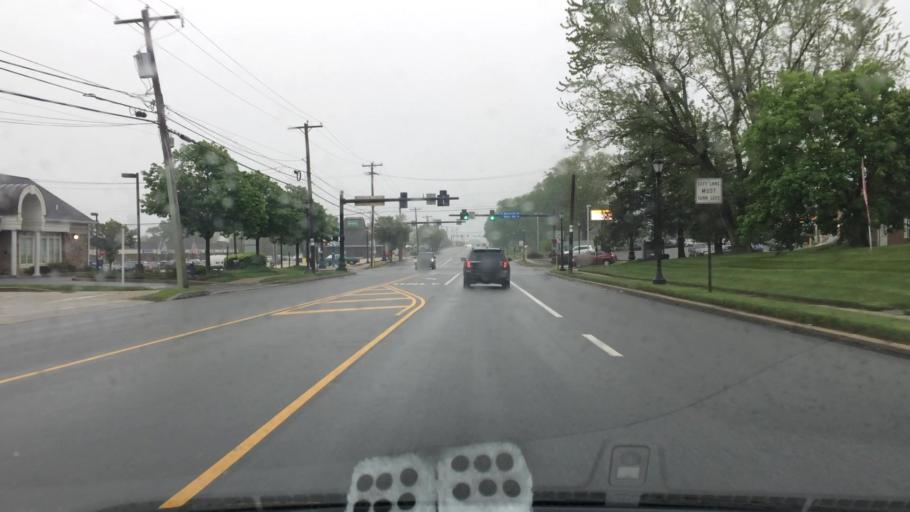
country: US
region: Pennsylvania
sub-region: Delaware County
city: Village Green-Green Ridge
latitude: 39.8649
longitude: -75.4280
